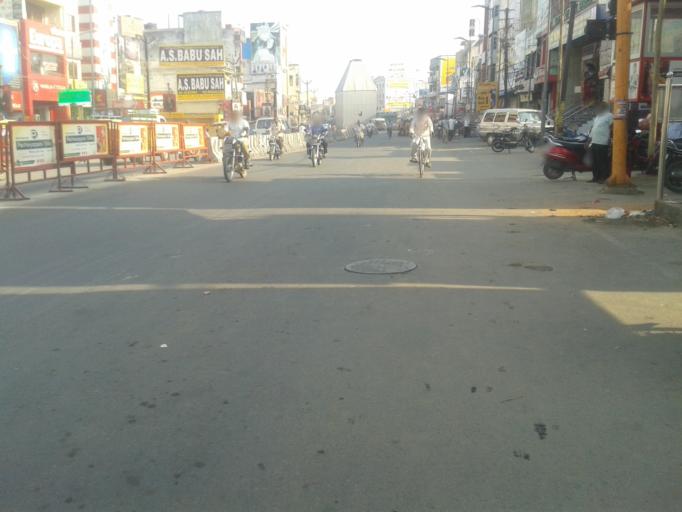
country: IN
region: Tamil Nadu
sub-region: Kancheepuram
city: Kanchipuram
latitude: 12.8268
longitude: 79.7079
